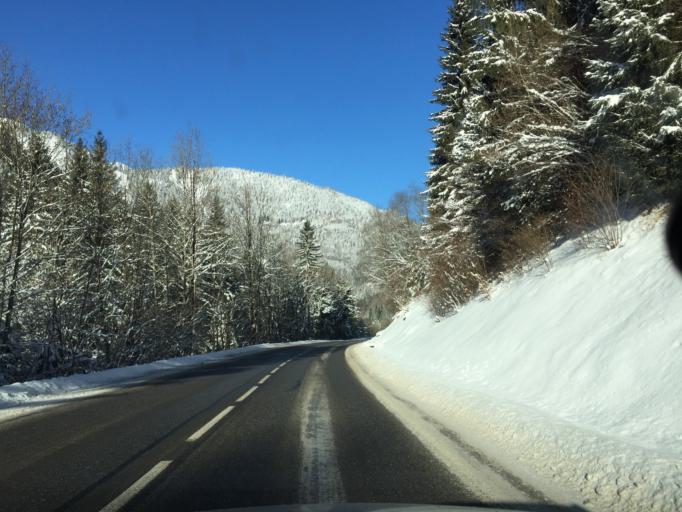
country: FR
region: Rhone-Alpes
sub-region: Departement de la Haute-Savoie
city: Abondance
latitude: 46.2901
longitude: 6.6868
